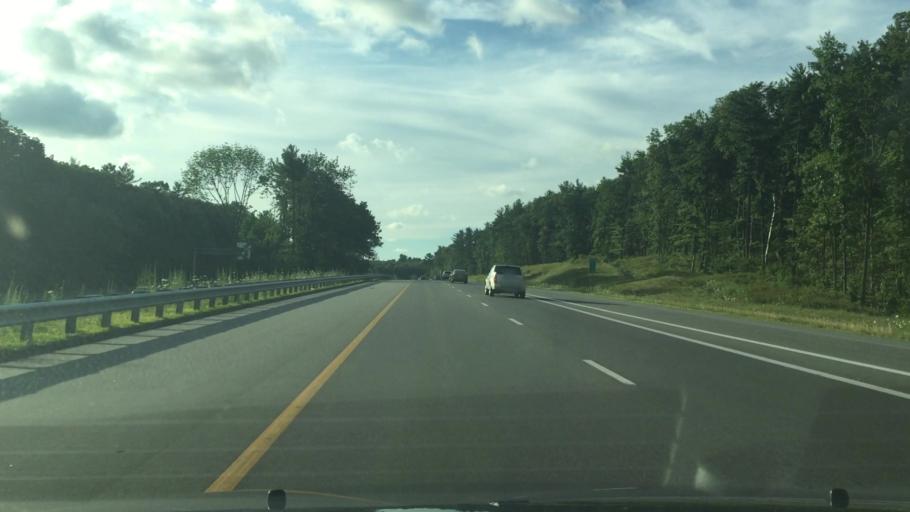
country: US
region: New Hampshire
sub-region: Rockingham County
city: Windham
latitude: 42.8283
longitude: -71.2921
